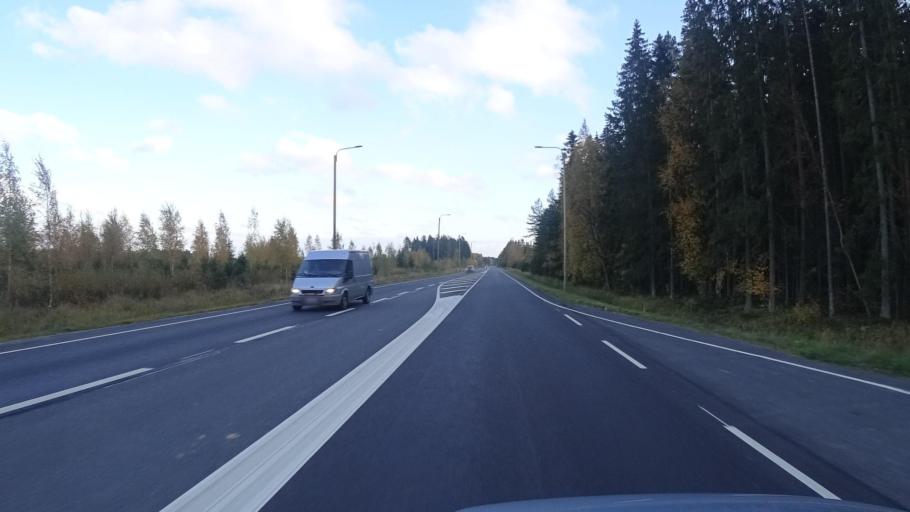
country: FI
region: Satakunta
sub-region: Rauma
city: Koeylioe
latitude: 61.0888
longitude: 22.2510
